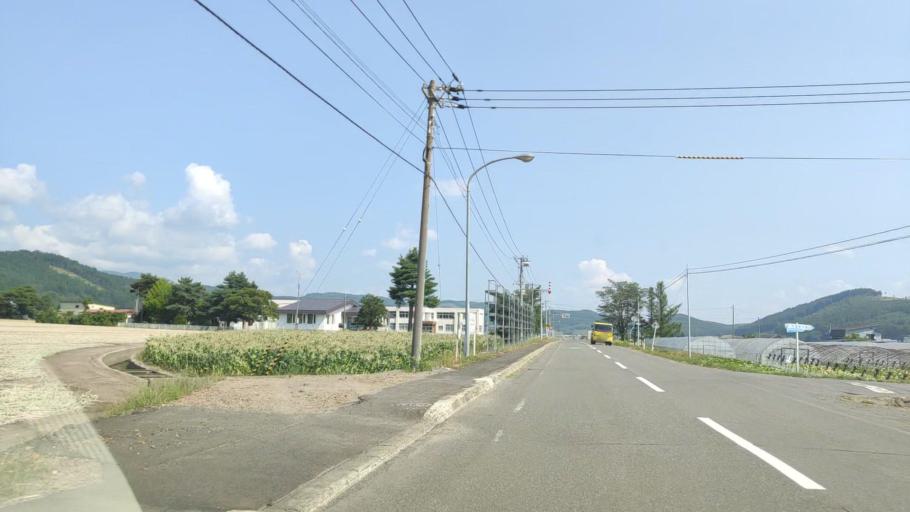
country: JP
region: Hokkaido
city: Shimo-furano
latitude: 43.3908
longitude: 142.3947
